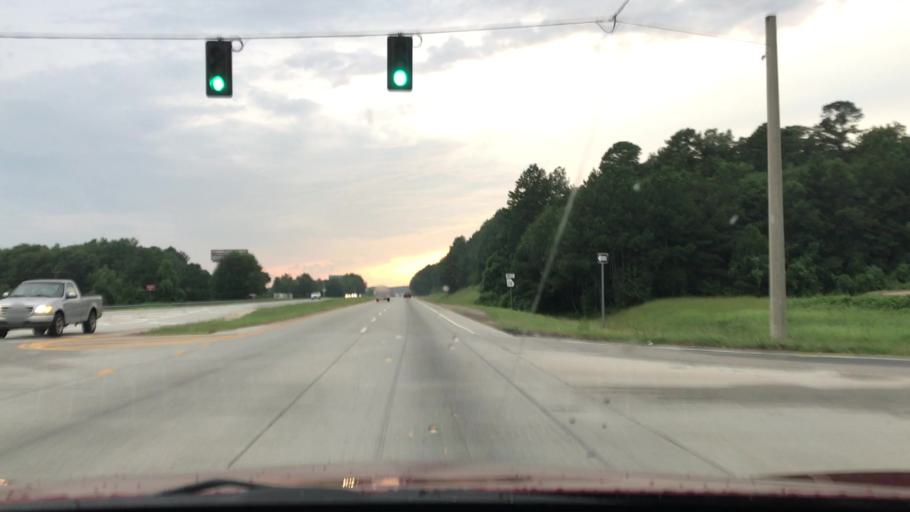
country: US
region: Georgia
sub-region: Barrow County
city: Auburn
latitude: 33.9678
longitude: -83.8197
